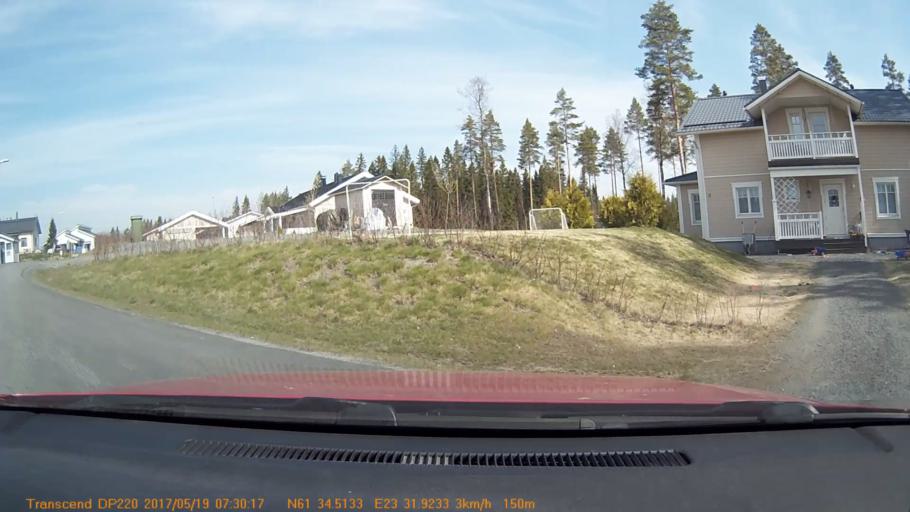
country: FI
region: Pirkanmaa
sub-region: Tampere
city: Yloejaervi
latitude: 61.5752
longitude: 23.5321
